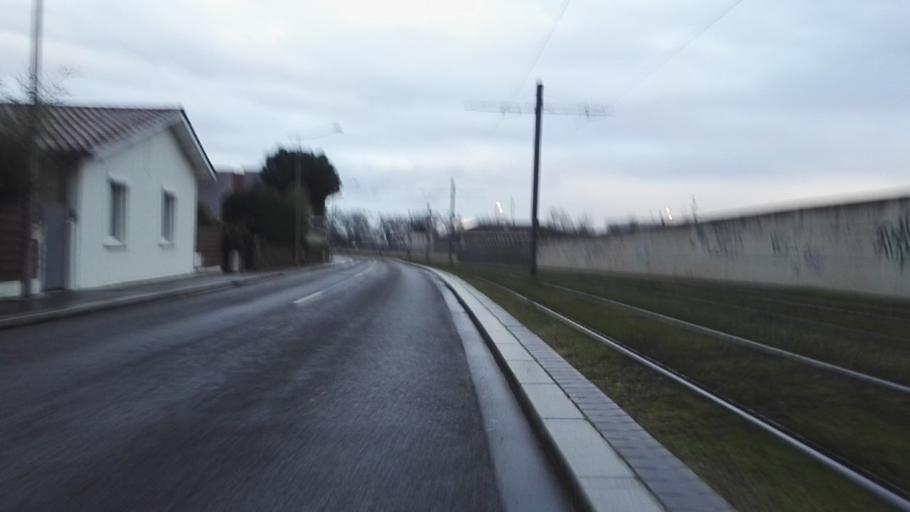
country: FR
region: Aquitaine
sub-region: Departement de la Gironde
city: Merignac
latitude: 44.8294
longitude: -0.6295
